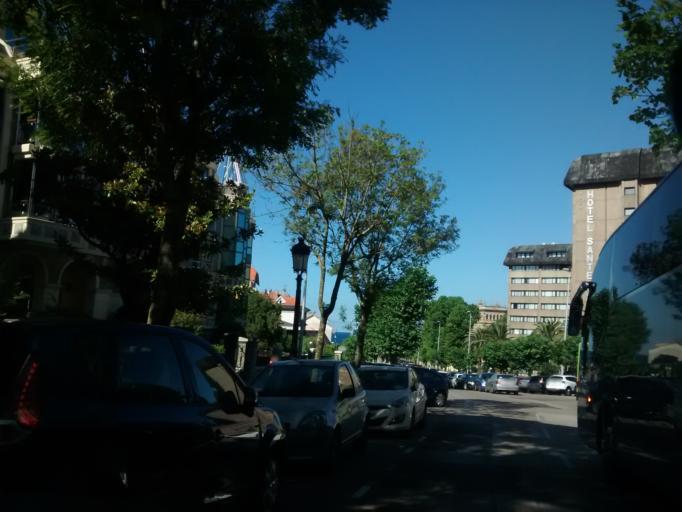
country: ES
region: Cantabria
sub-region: Provincia de Cantabria
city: Santander
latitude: 43.4696
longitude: -3.7843
